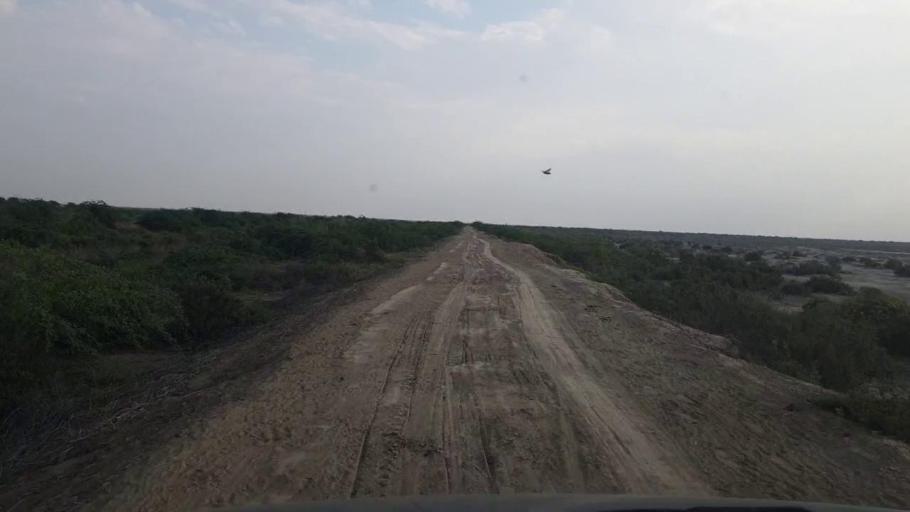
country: PK
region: Sindh
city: Badin
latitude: 24.4809
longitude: 68.6986
